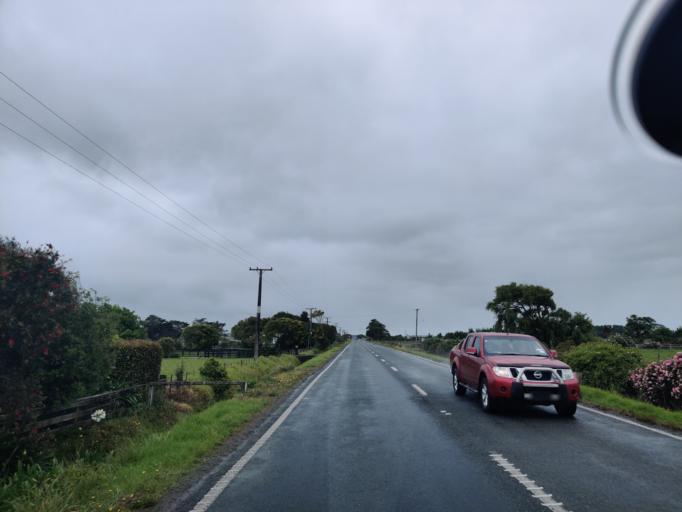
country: NZ
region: Northland
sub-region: Kaipara District
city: Dargaville
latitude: -35.9482
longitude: 173.8901
